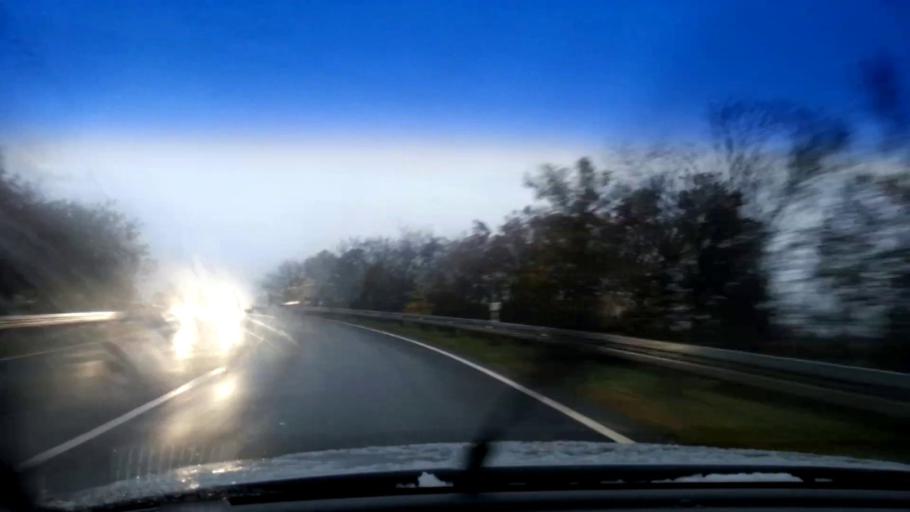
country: DE
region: Bavaria
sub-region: Upper Franconia
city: Oberhaid
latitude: 49.9335
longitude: 10.7989
